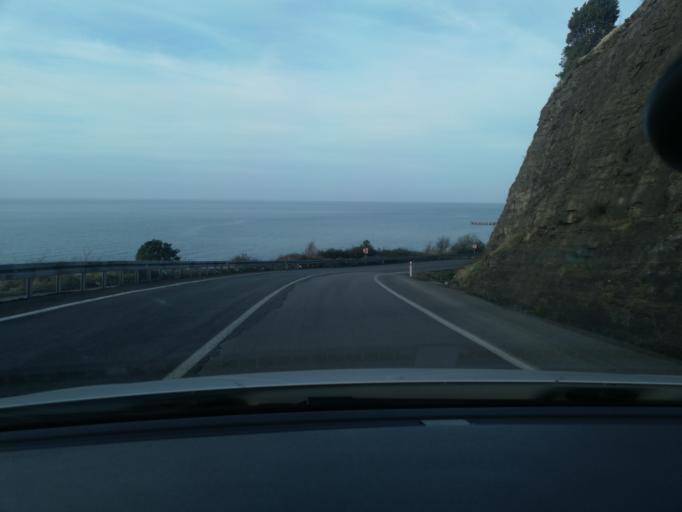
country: TR
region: Zonguldak
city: Tieum
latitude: 41.5516
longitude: 32.0062
